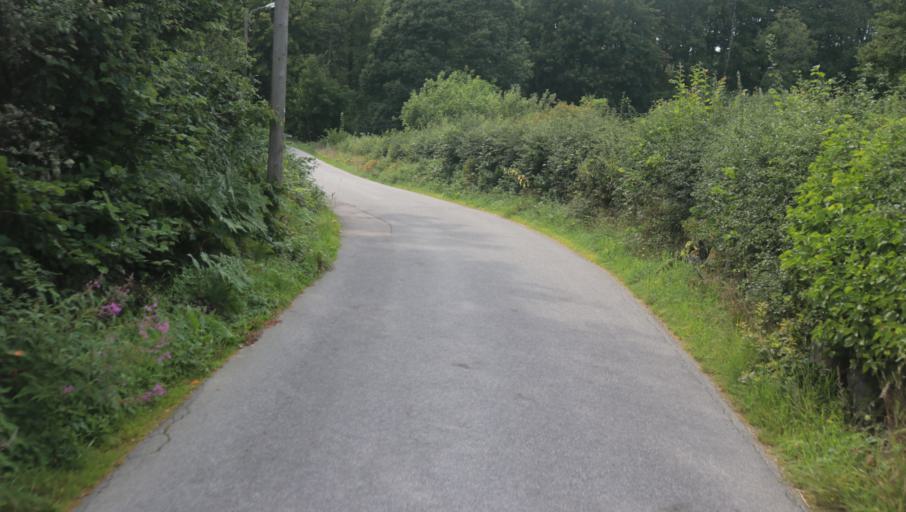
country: SE
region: Blekinge
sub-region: Karlshamns Kommun
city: Karlshamn
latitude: 56.2064
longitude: 14.8687
